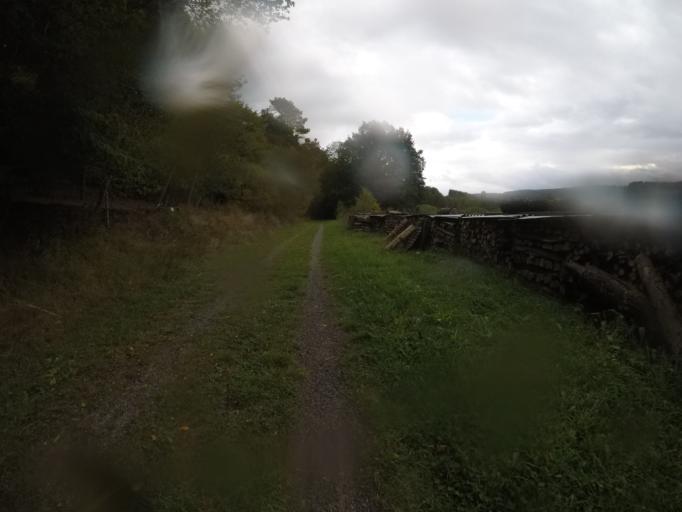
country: BE
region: Wallonia
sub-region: Province du Luxembourg
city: Fauvillers
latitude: 49.8742
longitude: 5.6845
